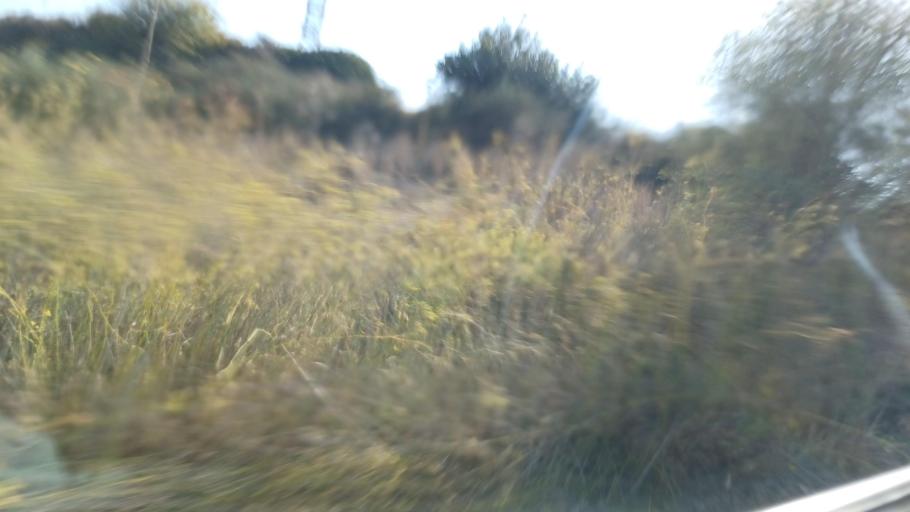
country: CY
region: Pafos
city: Polis
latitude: 35.0423
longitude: 32.4616
